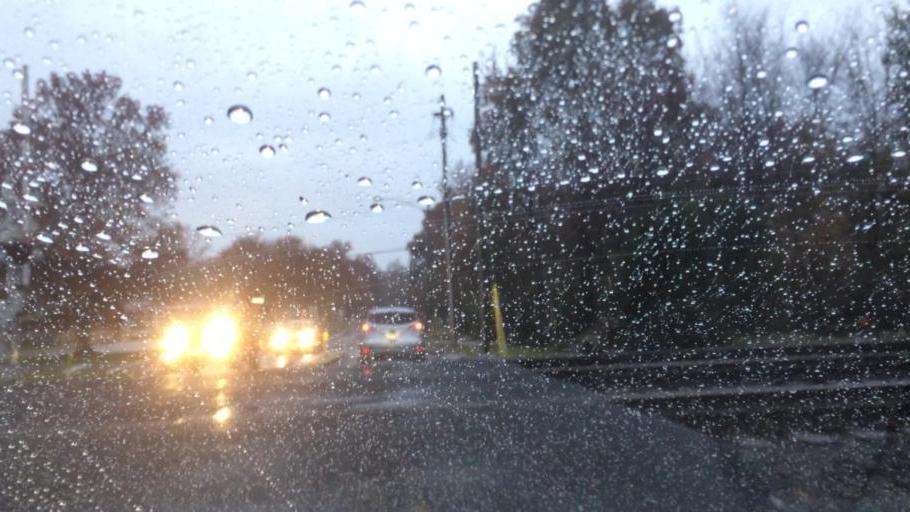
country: US
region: Ohio
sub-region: Cuyahoga County
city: Olmsted Falls
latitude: 41.3751
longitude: -81.9048
